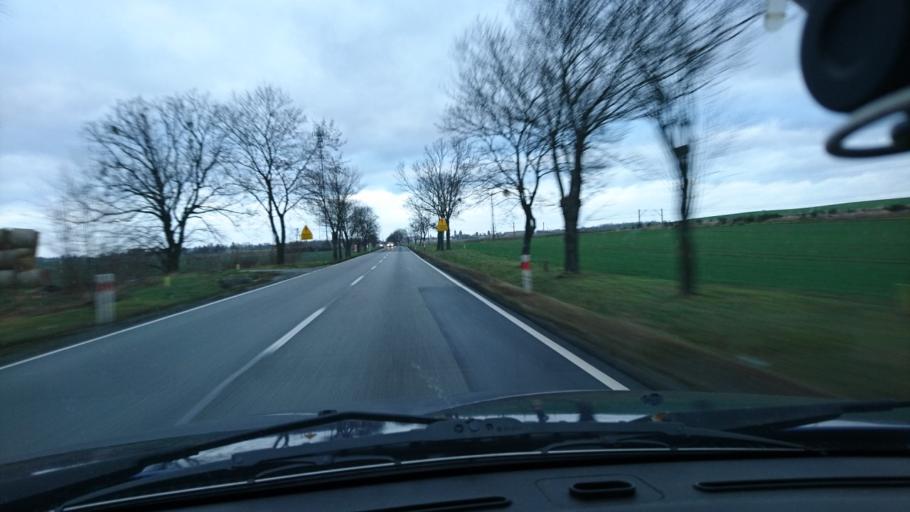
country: PL
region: Opole Voivodeship
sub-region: Powiat kluczborski
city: Byczyna
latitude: 51.0957
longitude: 18.2030
